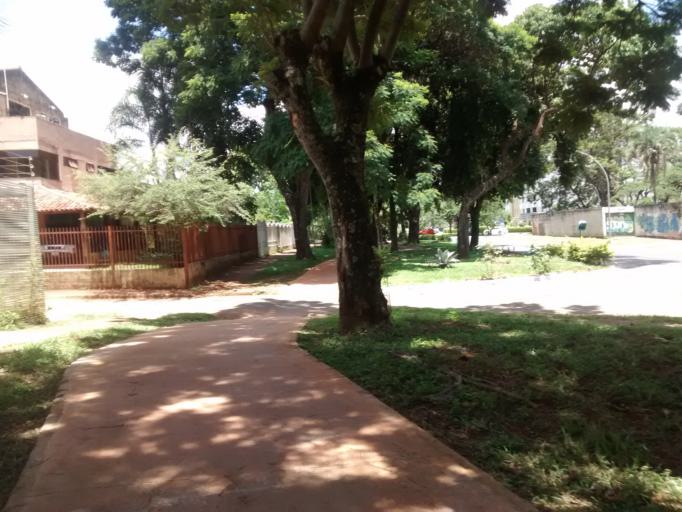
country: BR
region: Federal District
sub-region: Brasilia
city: Brasilia
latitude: -15.8179
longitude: -47.9182
